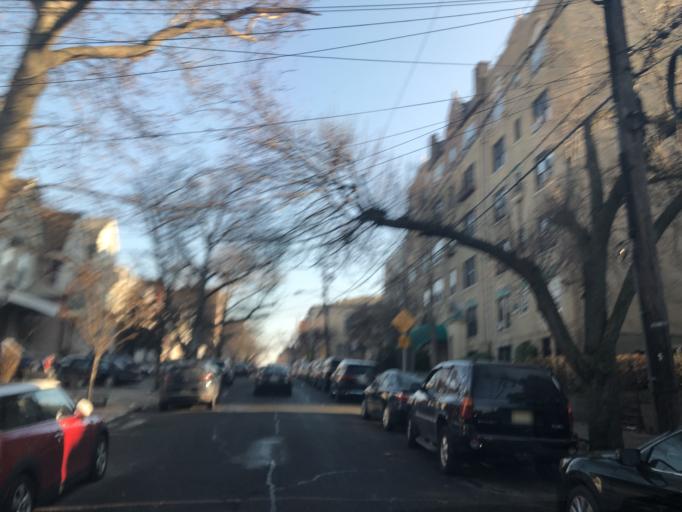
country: US
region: New Jersey
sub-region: Hudson County
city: Jersey City
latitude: 40.7239
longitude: -74.0771
